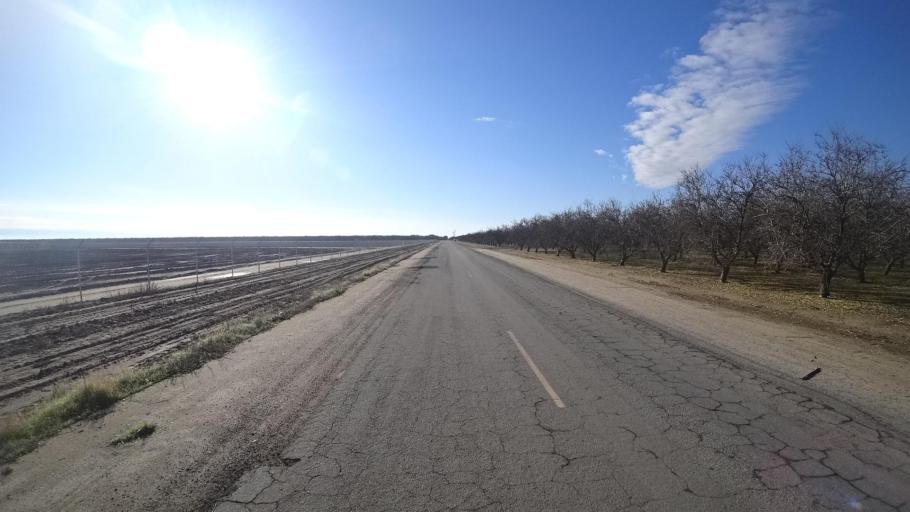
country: US
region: California
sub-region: Kern County
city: McFarland
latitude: 35.6931
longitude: -119.3120
